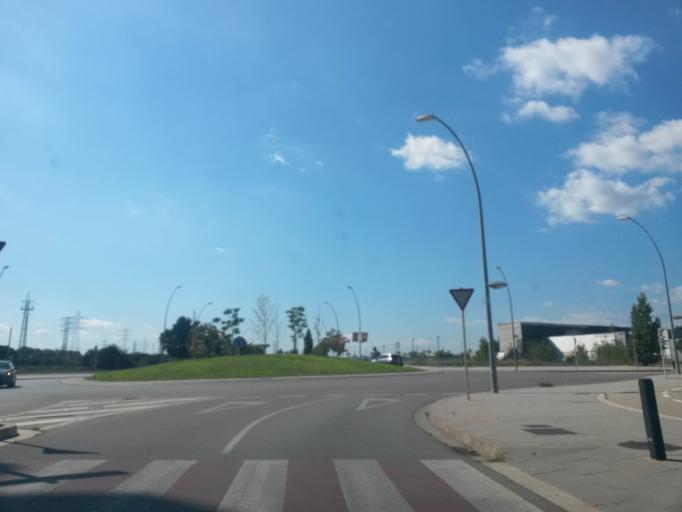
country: ES
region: Catalonia
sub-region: Provincia de Girona
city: Salt
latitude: 41.9712
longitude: 2.8001
